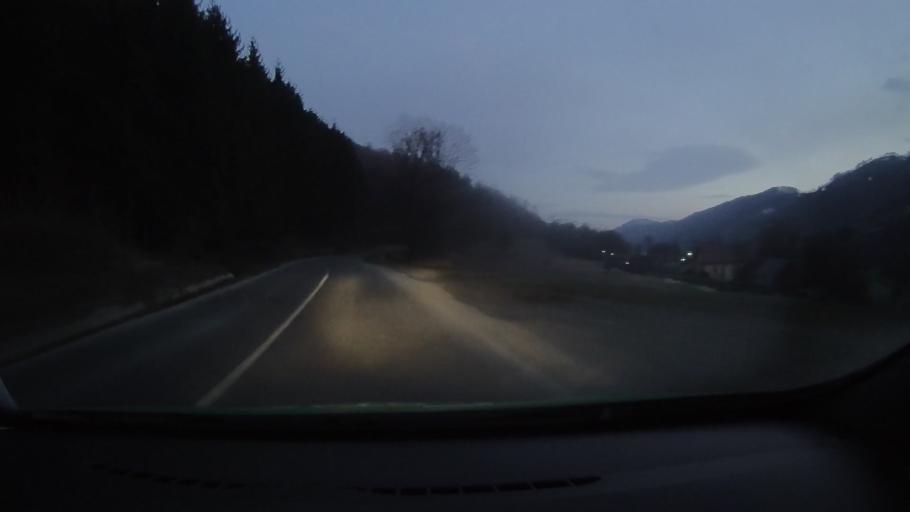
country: RO
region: Prahova
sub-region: Comuna Valea Doftanei
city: Tesila
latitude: 45.2745
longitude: 25.7317
